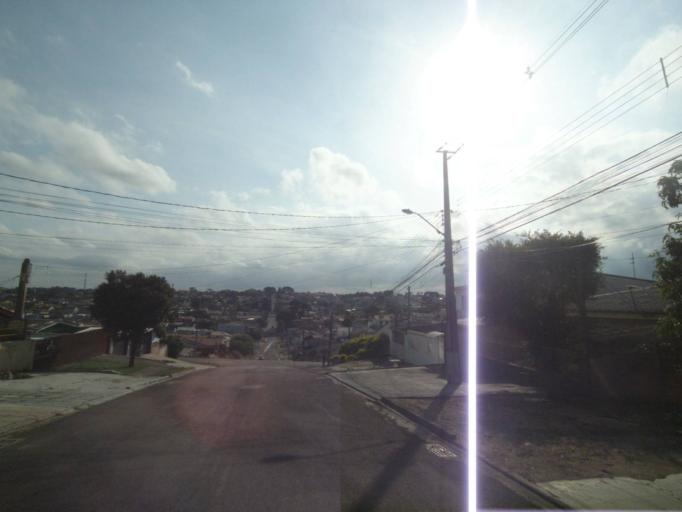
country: BR
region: Parana
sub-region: Pinhais
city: Pinhais
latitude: -25.4067
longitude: -49.1993
